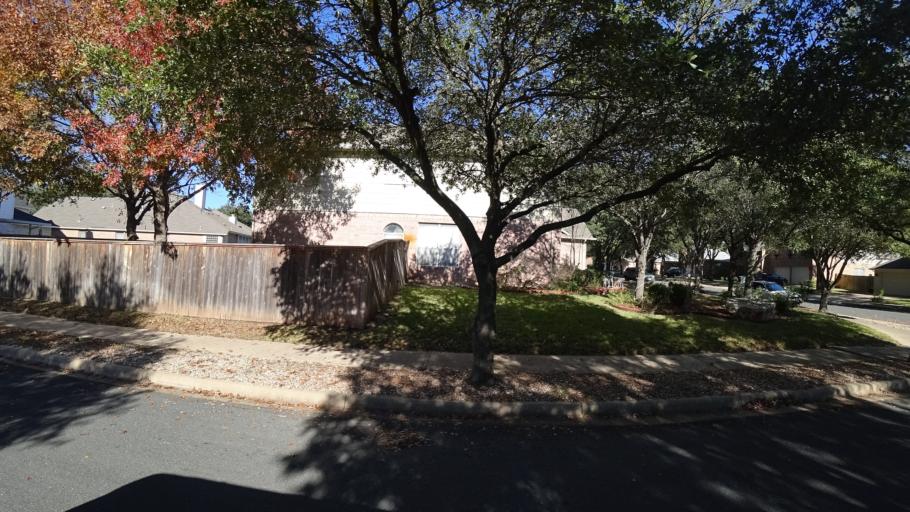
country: US
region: Texas
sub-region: Travis County
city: Wells Branch
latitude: 30.4271
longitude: -97.6929
